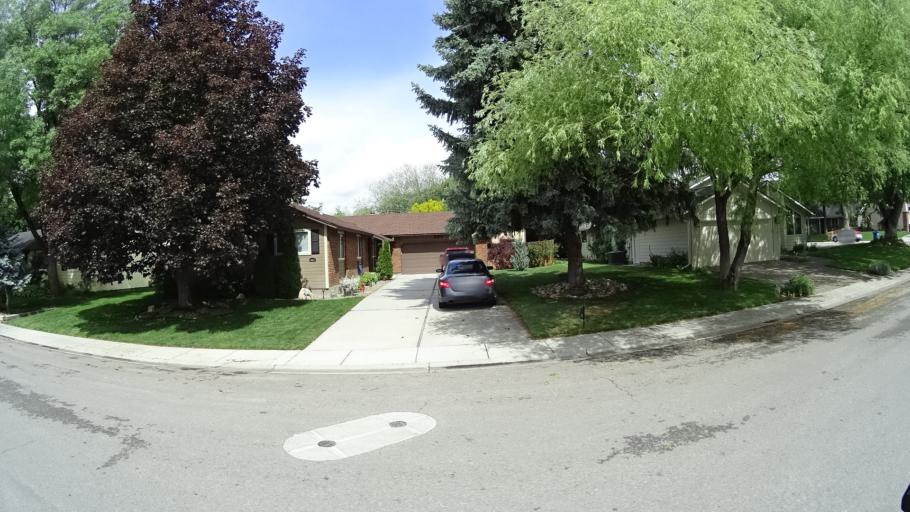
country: US
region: Idaho
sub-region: Ada County
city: Eagle
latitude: 43.7016
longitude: -116.3487
